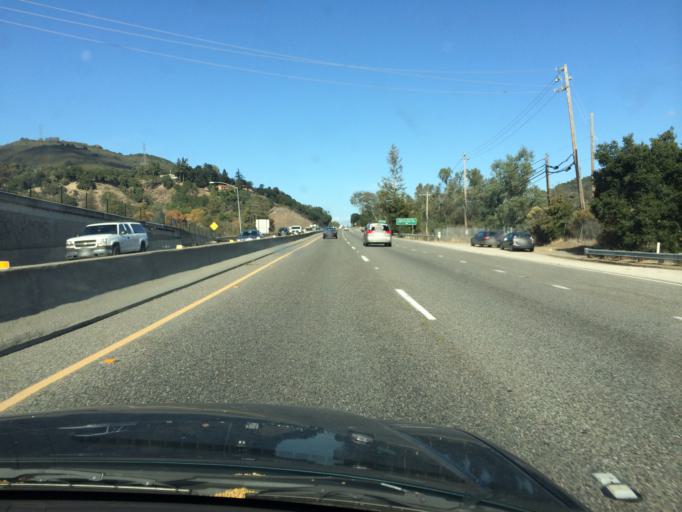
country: US
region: California
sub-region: Santa Clara County
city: Lexington Hills
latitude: 37.1940
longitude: -121.9939
